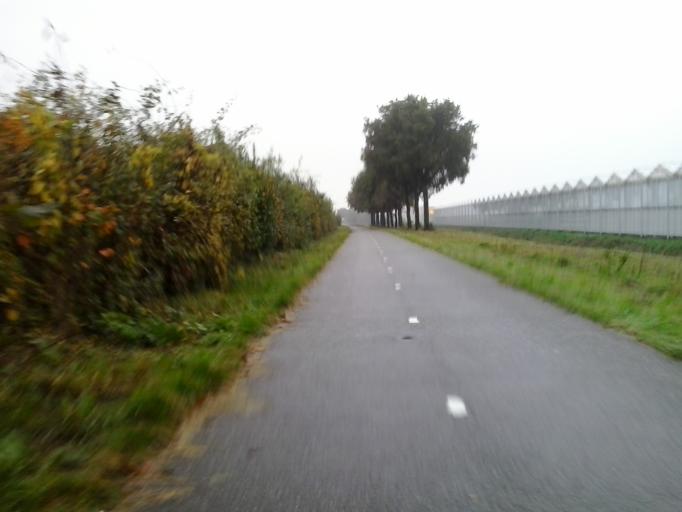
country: NL
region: South Holland
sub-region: Gemeente Lansingerland
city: Bergschenhoek
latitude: 52.0195
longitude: 4.5031
